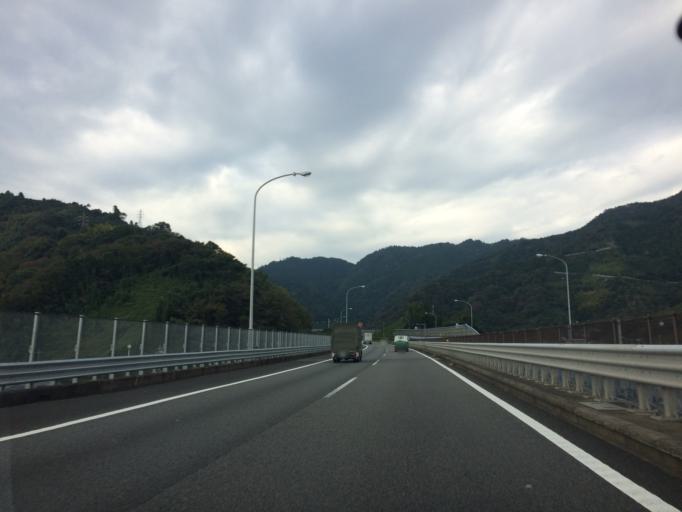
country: JP
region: Shizuoka
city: Shizuoka-shi
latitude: 34.9268
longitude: 138.3554
